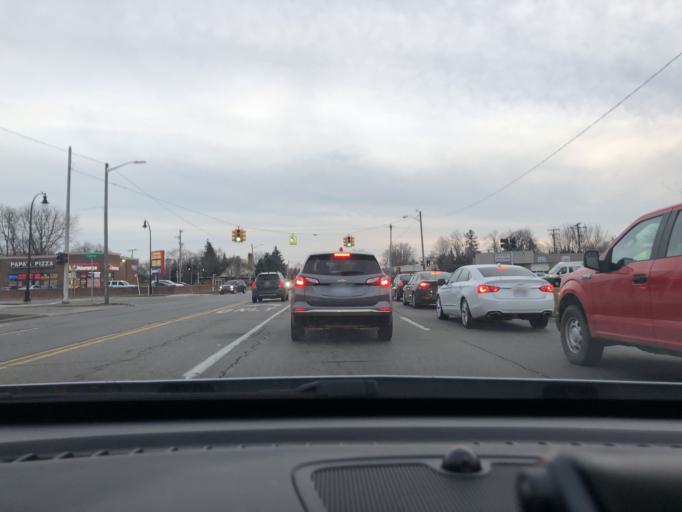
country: US
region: Michigan
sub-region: Wayne County
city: Allen Park
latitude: 42.2570
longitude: -83.2313
